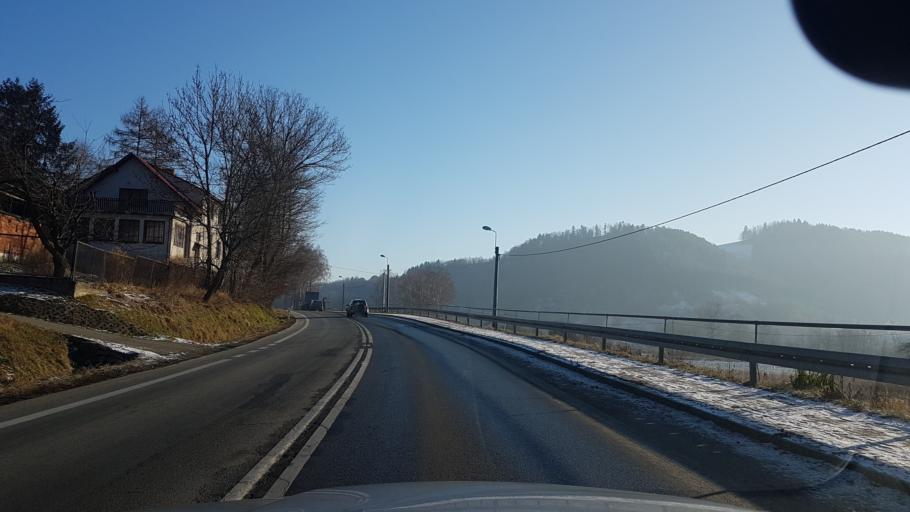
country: PL
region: Lesser Poland Voivodeship
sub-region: Powiat nowosadecki
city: Olszana
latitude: 49.5277
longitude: 20.5064
